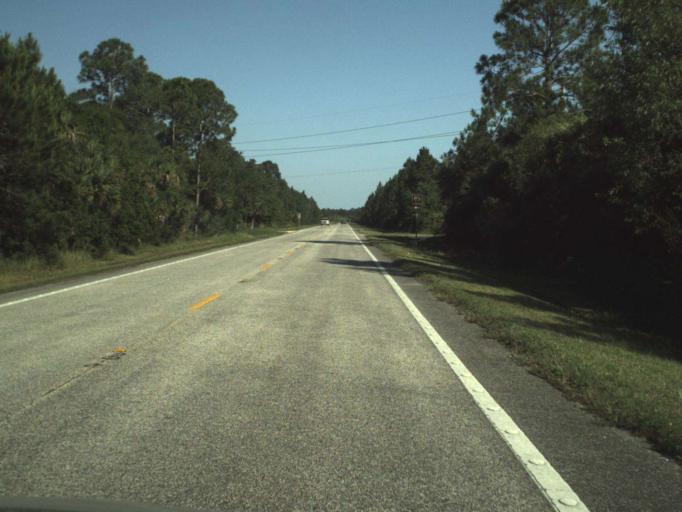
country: US
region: Florida
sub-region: Brevard County
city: Mims
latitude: 28.6729
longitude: -80.9734
